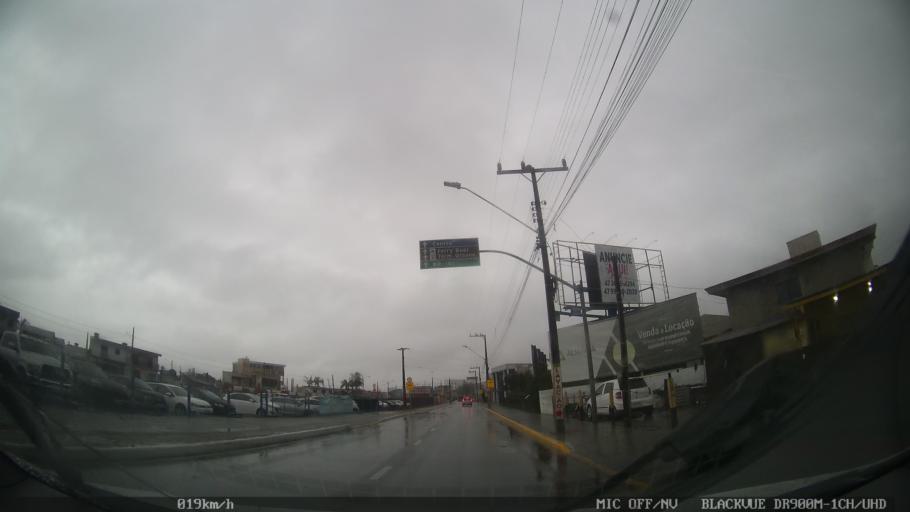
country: BR
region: Santa Catarina
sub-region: Navegantes
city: Navegantes
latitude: -26.8829
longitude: -48.6516
